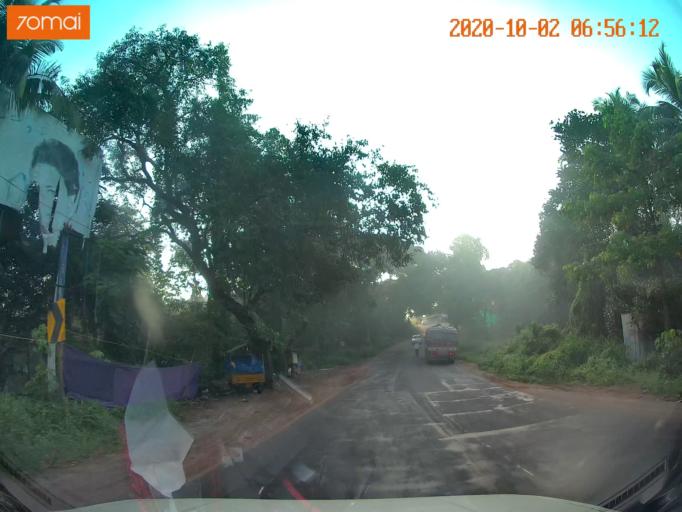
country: IN
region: Kerala
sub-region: Malappuram
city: Tirur
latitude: 10.8682
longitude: 76.0435
